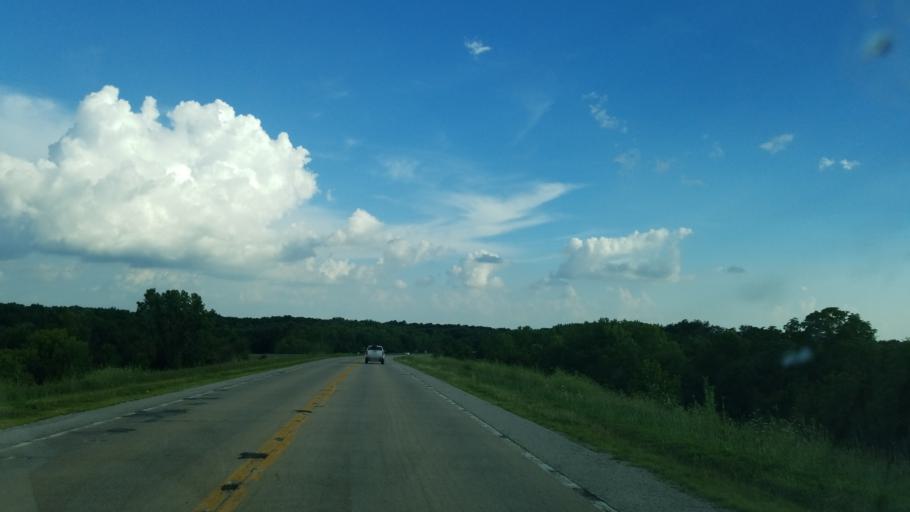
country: US
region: Illinois
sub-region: Marion County
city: Central City
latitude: 38.5793
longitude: -89.1084
